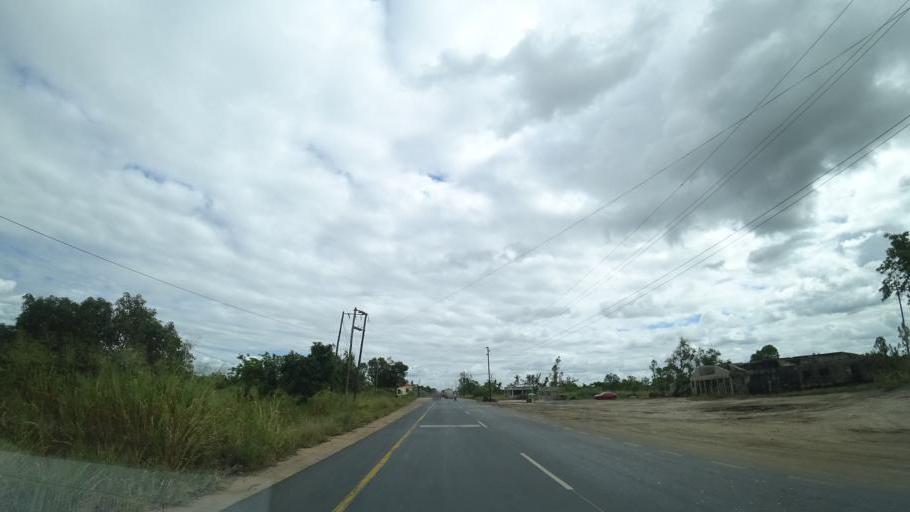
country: MZ
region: Sofala
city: Dondo
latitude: -19.5088
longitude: 34.6094
